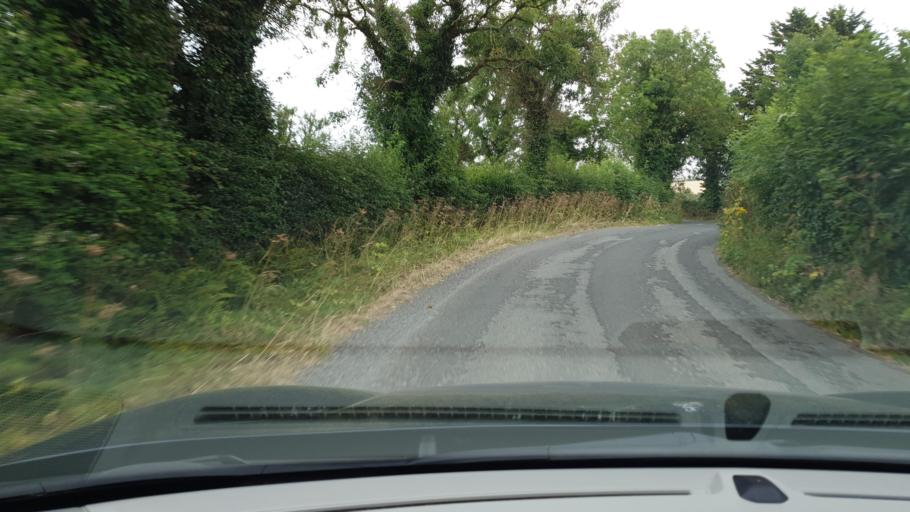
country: IE
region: Leinster
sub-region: An Mhi
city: Stamullin
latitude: 53.5866
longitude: -6.3276
